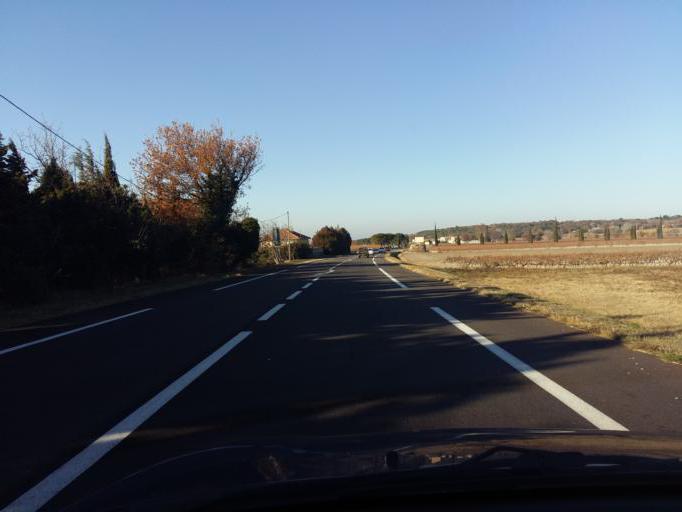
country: FR
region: Provence-Alpes-Cote d'Azur
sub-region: Departement du Vaucluse
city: Valreas
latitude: 44.3891
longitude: 4.9685
